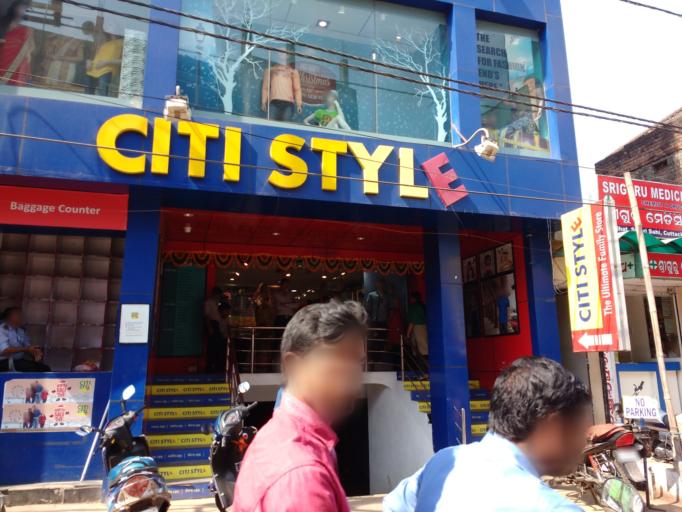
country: IN
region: Odisha
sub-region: Cuttack
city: Cuttack
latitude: 20.4675
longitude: 85.8879
